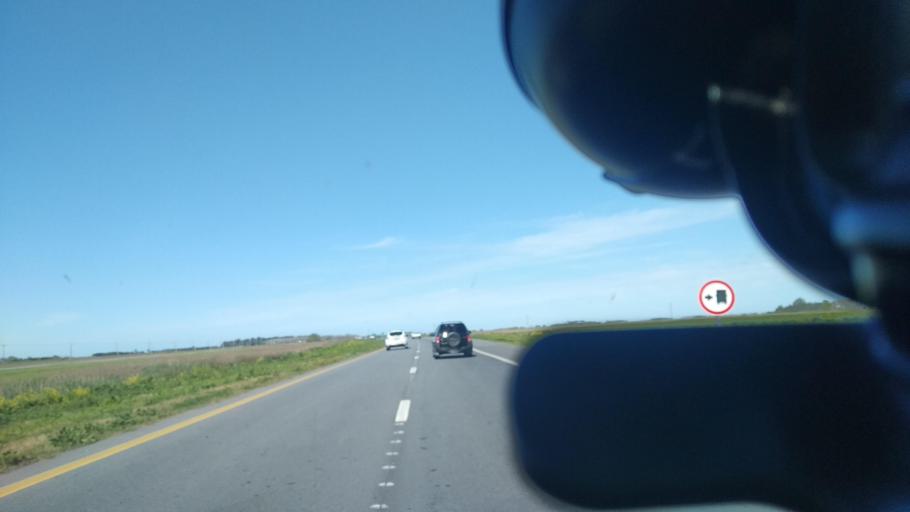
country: AR
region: Buenos Aires
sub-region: Partido de General Lavalle
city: General Lavalle
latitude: -36.4312
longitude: -56.9122
